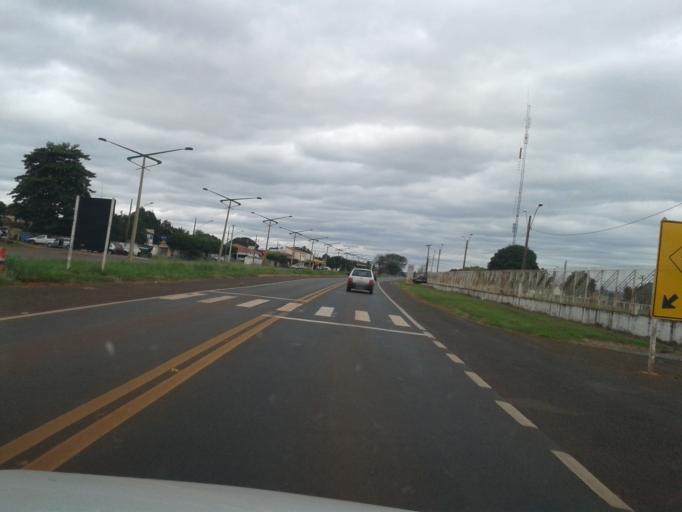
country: BR
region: Minas Gerais
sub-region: Campina Verde
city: Campina Verde
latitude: -19.5400
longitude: -49.4900
